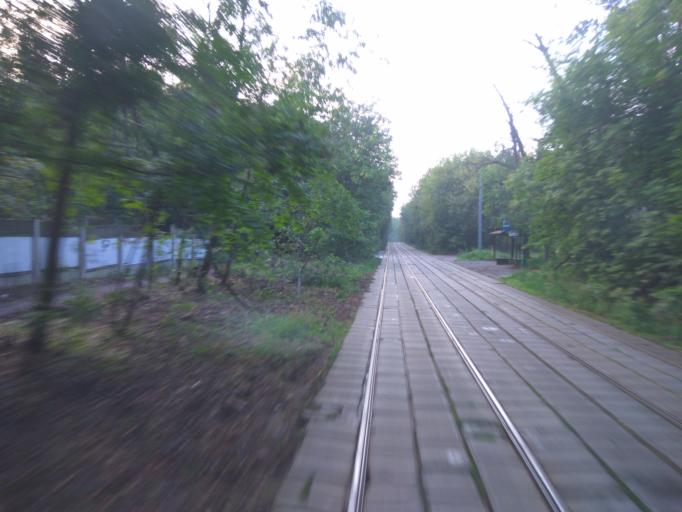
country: RU
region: Moscow
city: Sokol'niki
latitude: 55.8083
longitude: 37.6885
